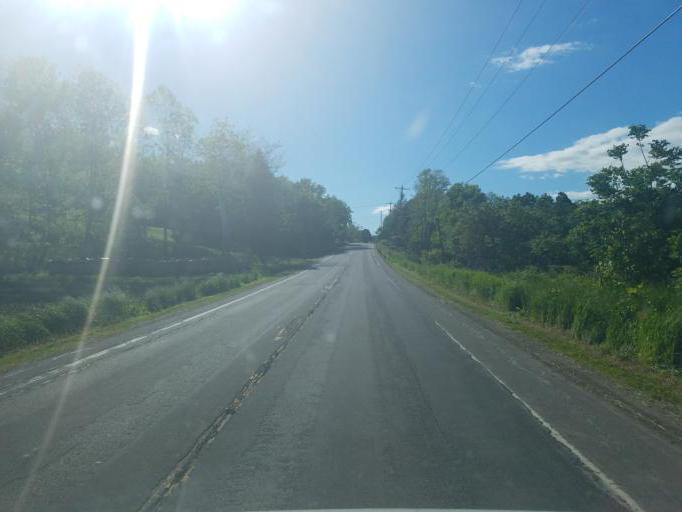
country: US
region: New York
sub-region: Herkimer County
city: Little Falls
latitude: 43.0051
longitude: -74.7818
